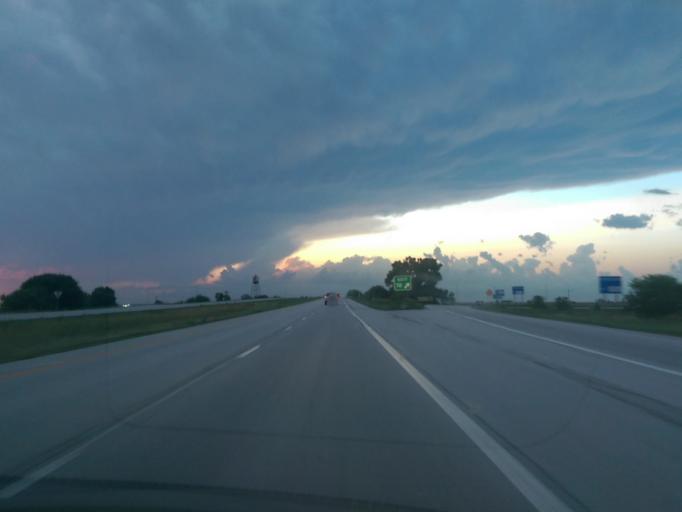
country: US
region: Nebraska
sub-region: Otoe County
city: Nebraska City
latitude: 40.6856
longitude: -95.7802
